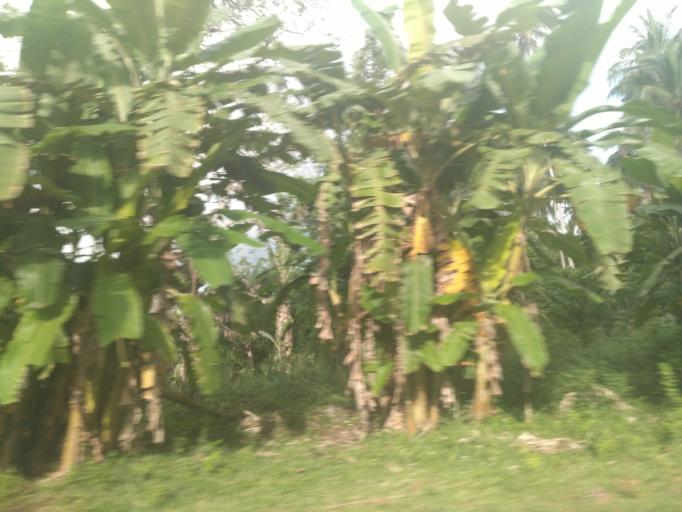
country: TZ
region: Zanzibar Central/South
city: Koani
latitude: -6.1069
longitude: 39.3017
